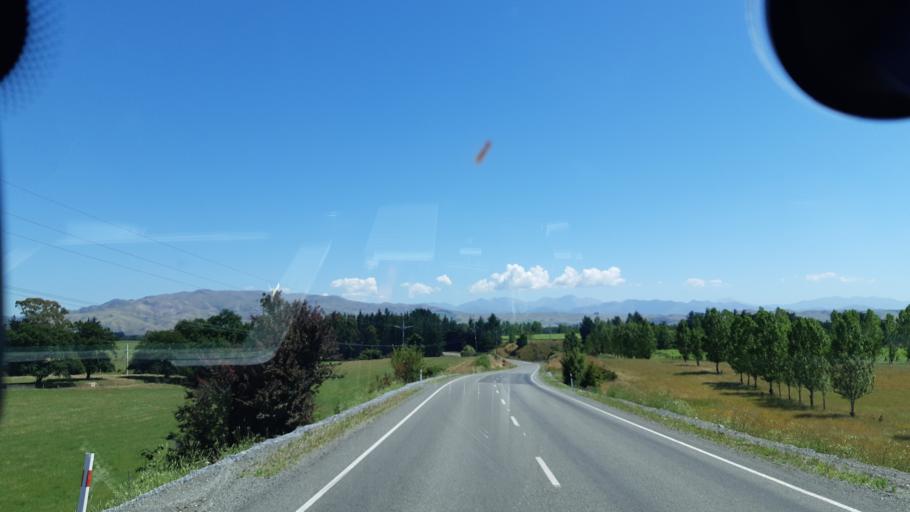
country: NZ
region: Canterbury
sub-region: Kaikoura District
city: Kaikoura
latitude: -42.7556
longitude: 173.2742
